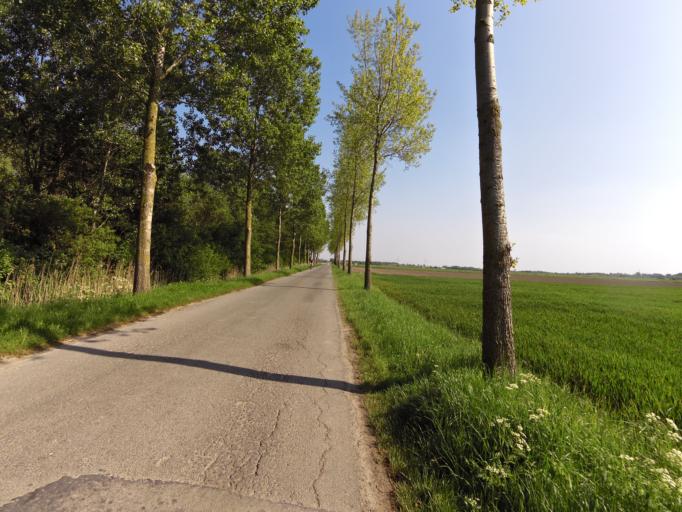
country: BE
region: Flanders
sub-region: Provincie West-Vlaanderen
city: Ostend
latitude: 51.1961
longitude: 2.9218
